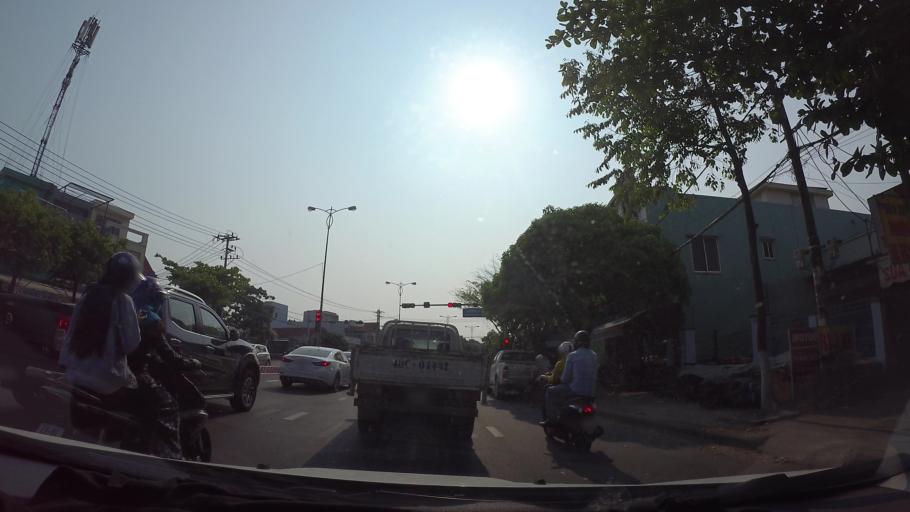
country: VN
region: Da Nang
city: Cam Le
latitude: 16.0142
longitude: 108.1989
